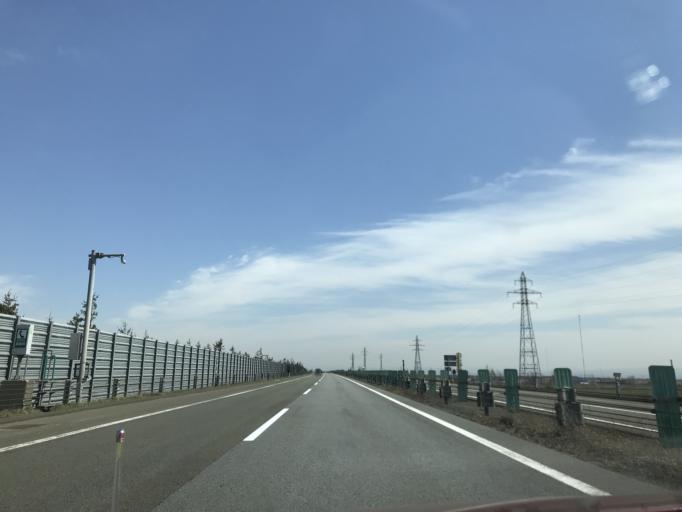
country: JP
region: Hokkaido
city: Ebetsu
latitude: 43.0867
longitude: 141.5638
